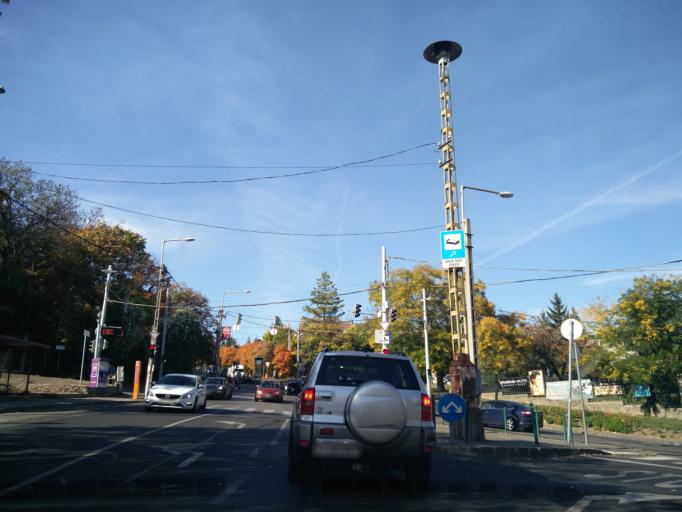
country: HU
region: Budapest
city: Budapest XII. keruelet
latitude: 47.4993
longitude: 19.0089
